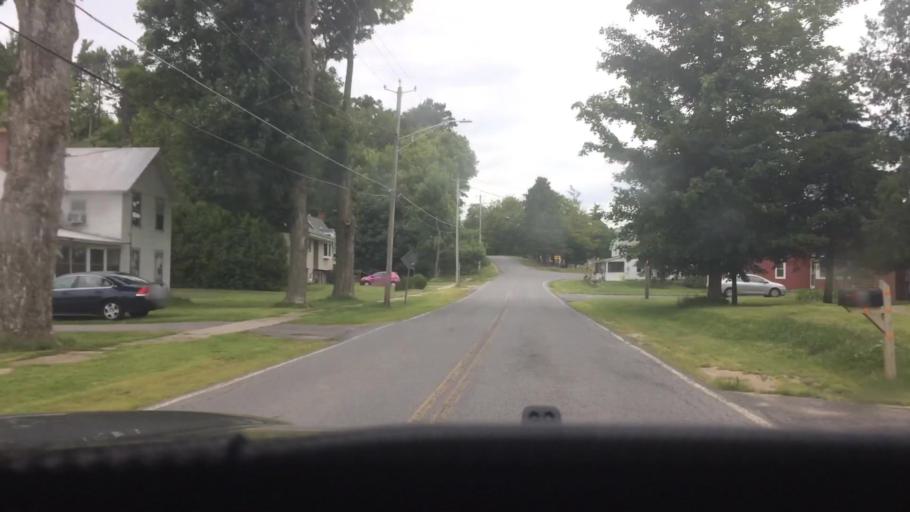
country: US
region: New York
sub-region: St. Lawrence County
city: Hannawa Falls
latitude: 44.5554
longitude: -74.9298
